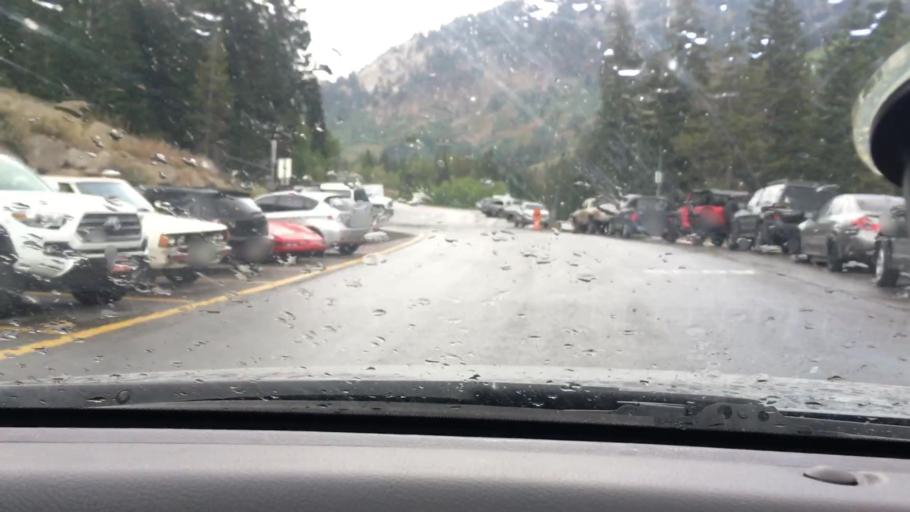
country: US
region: Utah
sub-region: Salt Lake County
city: Granite
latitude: 40.5793
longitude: -111.6651
